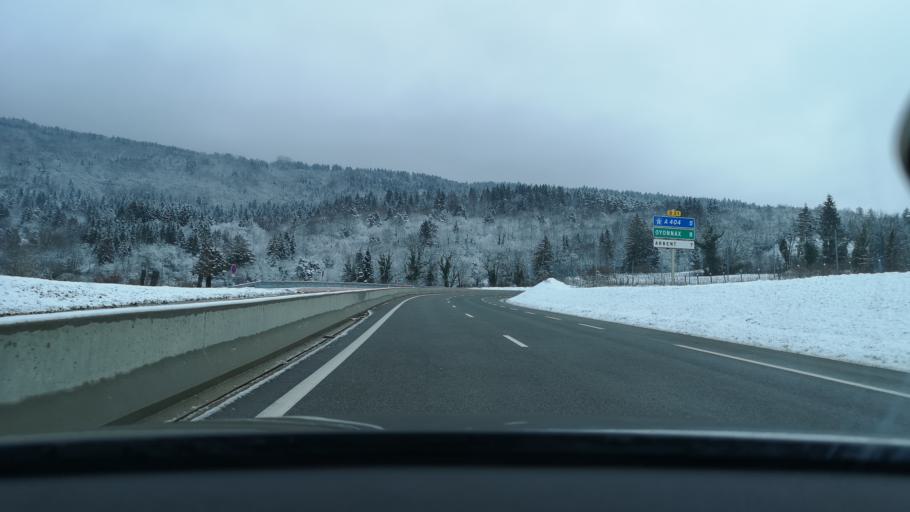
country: FR
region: Rhone-Alpes
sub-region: Departement de l'Ain
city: Dortan
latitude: 46.3236
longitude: 5.6722
